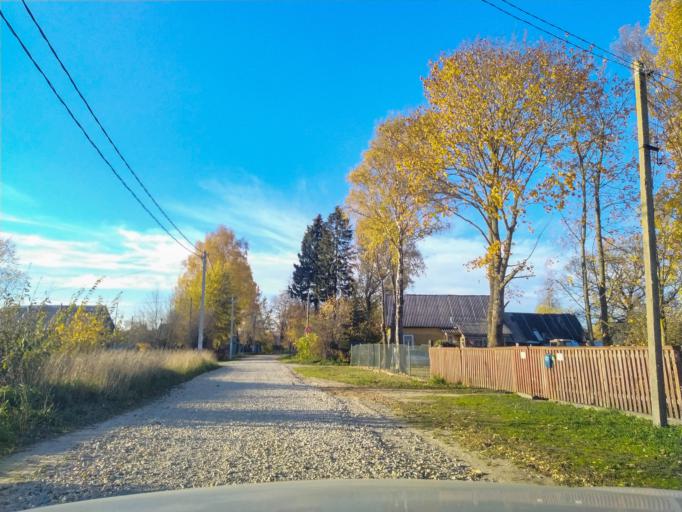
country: RU
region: Leningrad
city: Siverskiy
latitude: 59.3233
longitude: 30.0457
